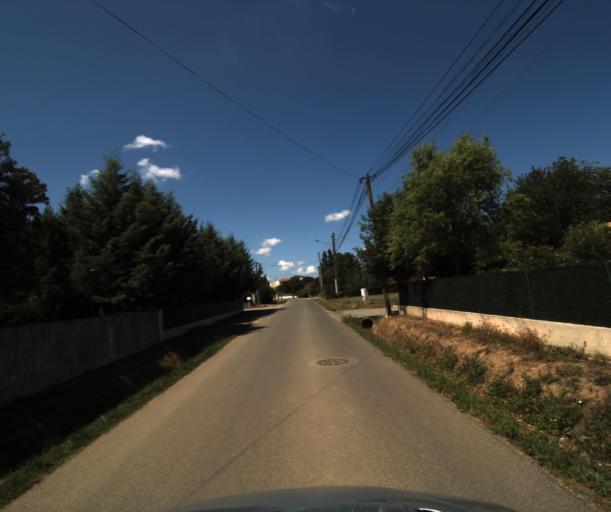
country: FR
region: Midi-Pyrenees
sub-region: Departement de la Haute-Garonne
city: Eaunes
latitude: 43.4250
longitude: 1.3424
